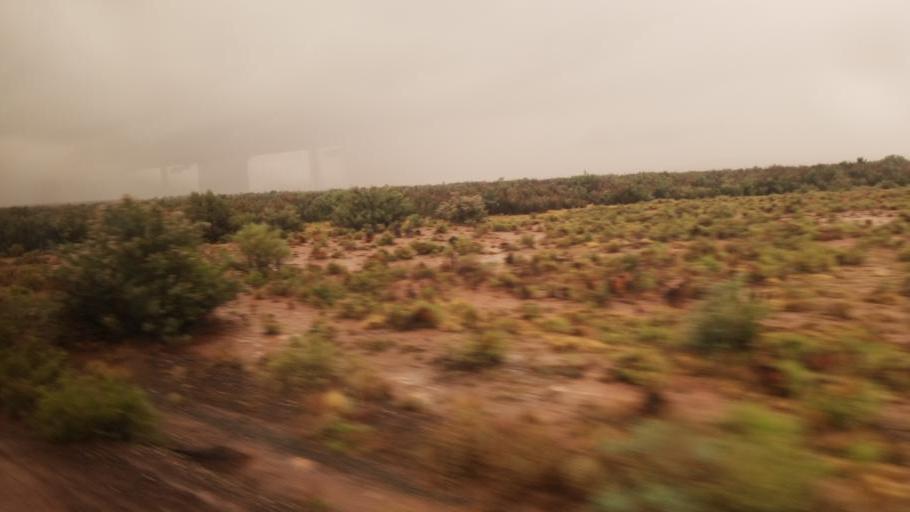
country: US
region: Arizona
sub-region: Navajo County
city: Joseph City
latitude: 34.9674
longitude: -110.4641
